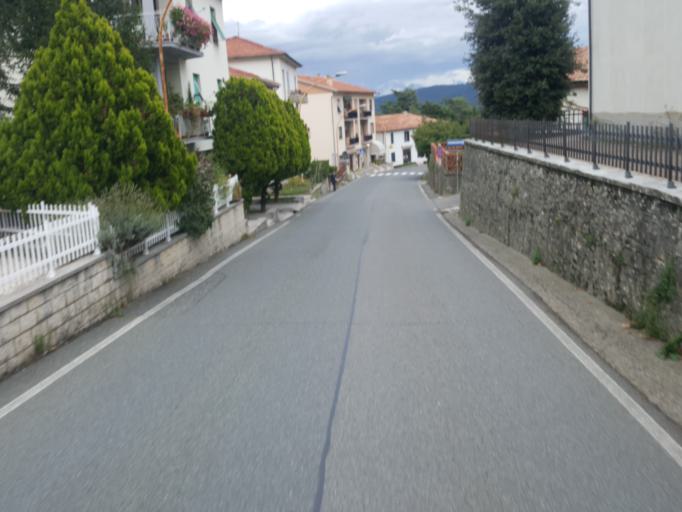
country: IT
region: Tuscany
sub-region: Province of Pisa
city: Castelnuovo di Val di Cecina
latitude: 43.2104
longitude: 10.9014
